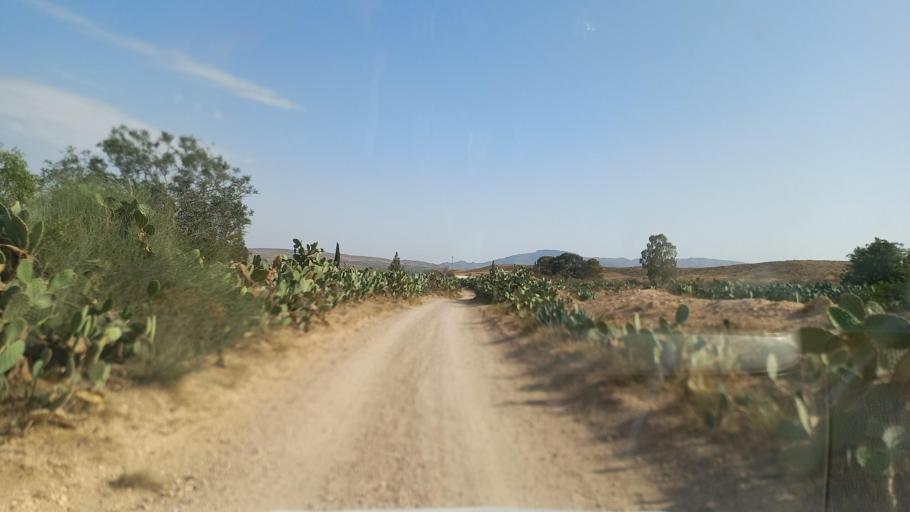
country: TN
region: Al Qasrayn
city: Kasserine
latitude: 35.2535
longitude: 8.9284
